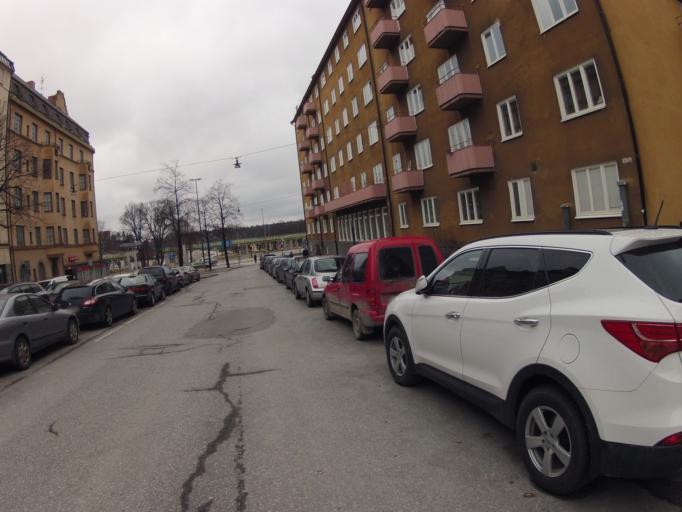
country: SE
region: Stockholm
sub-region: Stockholms Kommun
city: Stockholm
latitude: 59.3493
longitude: 18.0450
